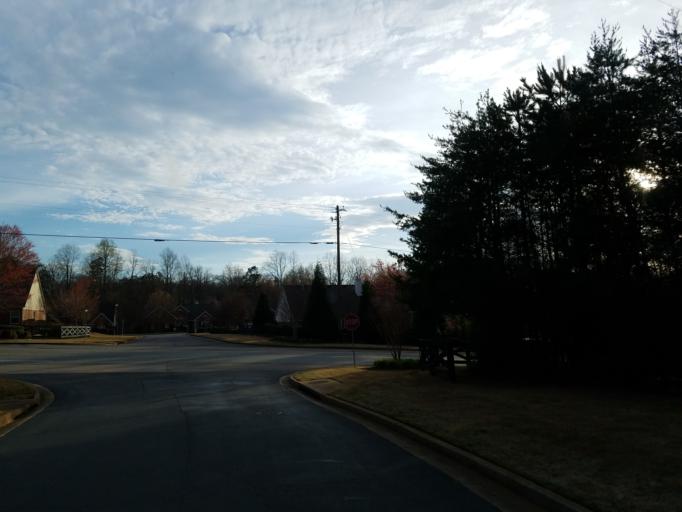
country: US
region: Georgia
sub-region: Dawson County
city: Dawsonville
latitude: 34.4291
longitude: -84.1242
